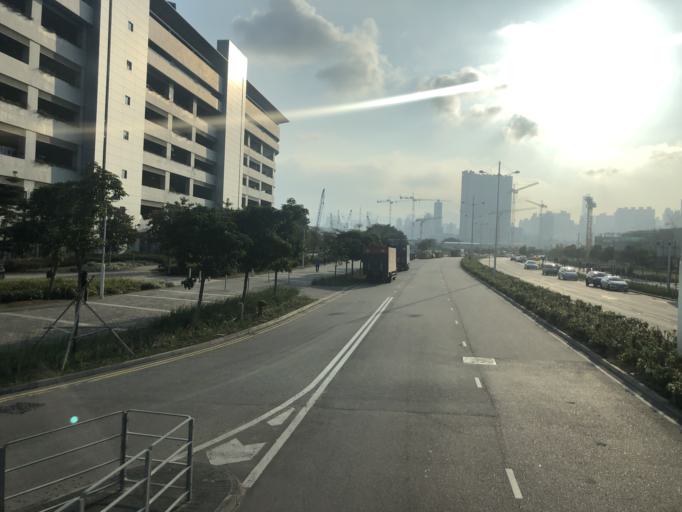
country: HK
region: Kowloon City
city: Kowloon
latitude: 22.3272
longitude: 114.2037
